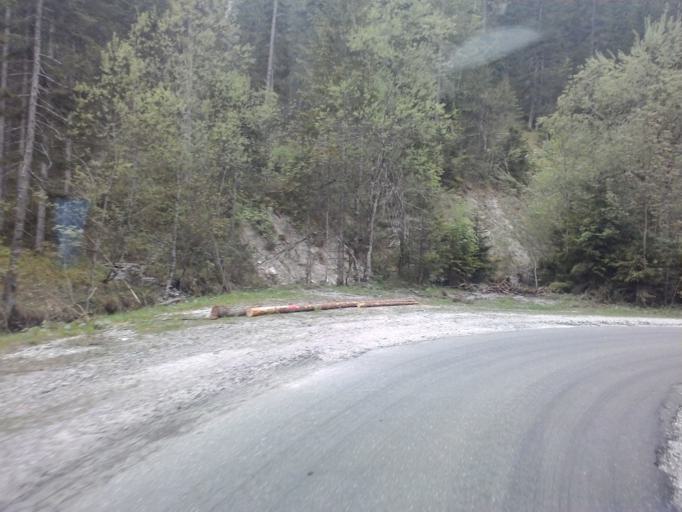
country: AT
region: Styria
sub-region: Politischer Bezirk Liezen
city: Wildalpen
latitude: 47.7002
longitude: 14.9970
